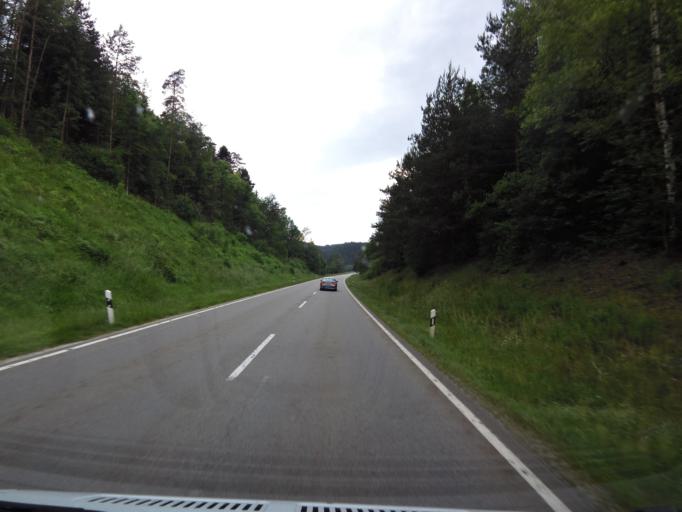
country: DE
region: Bavaria
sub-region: Lower Bavaria
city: Hutthurm
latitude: 48.6845
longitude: 13.4526
